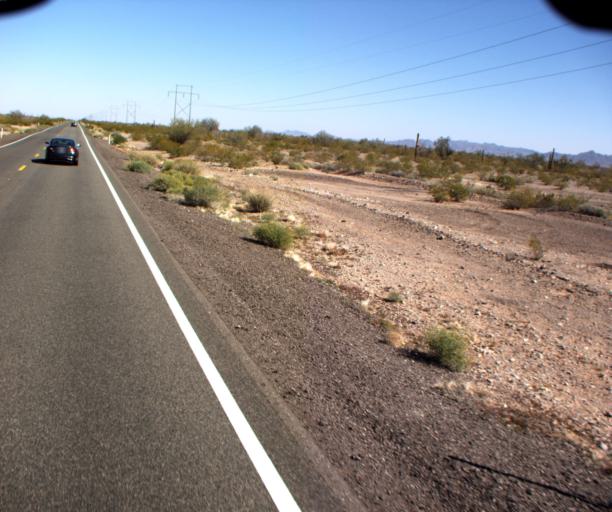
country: US
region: Arizona
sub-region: La Paz County
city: Quartzsite
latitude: 33.5591
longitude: -114.2170
